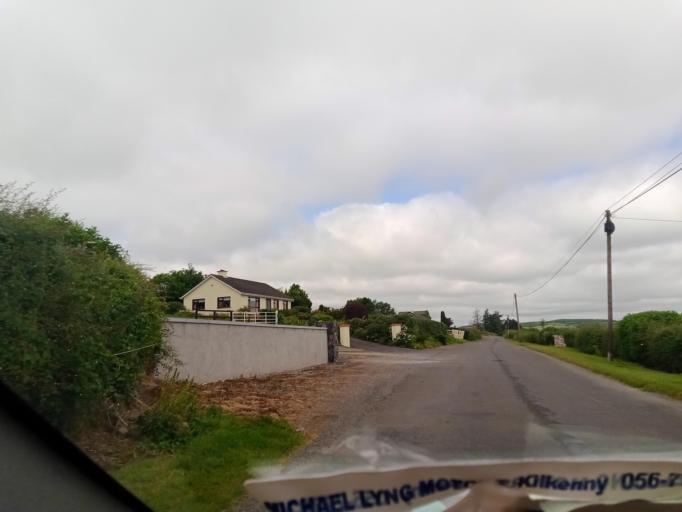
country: IE
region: Leinster
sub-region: Kilkenny
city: Ballyragget
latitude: 52.7556
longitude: -7.4465
